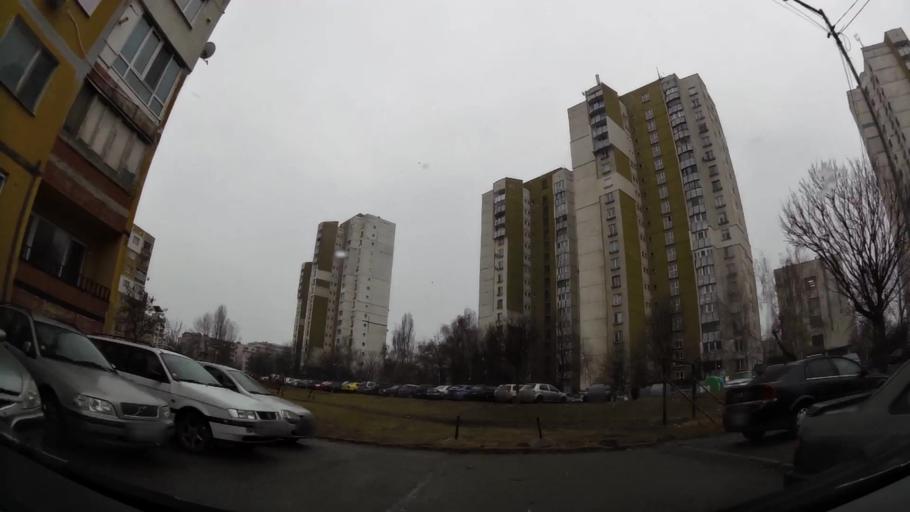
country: BG
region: Sofia-Capital
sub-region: Stolichna Obshtina
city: Sofia
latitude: 42.6652
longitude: 23.3804
